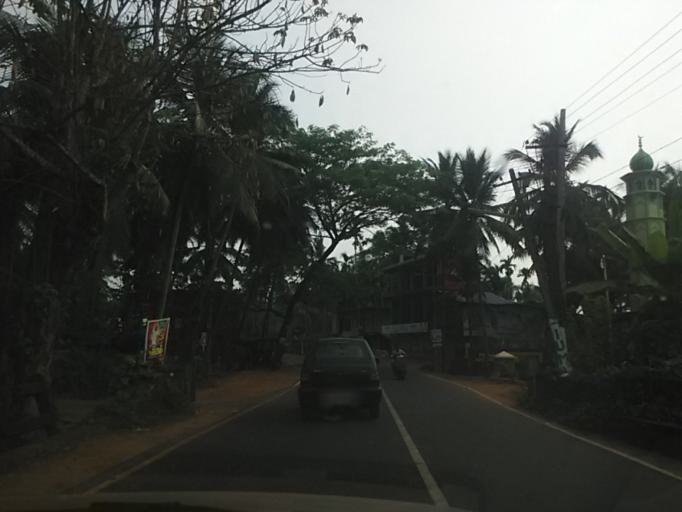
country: IN
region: Kerala
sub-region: Kozhikode
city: Naduvannur
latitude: 11.5007
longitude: 75.7726
